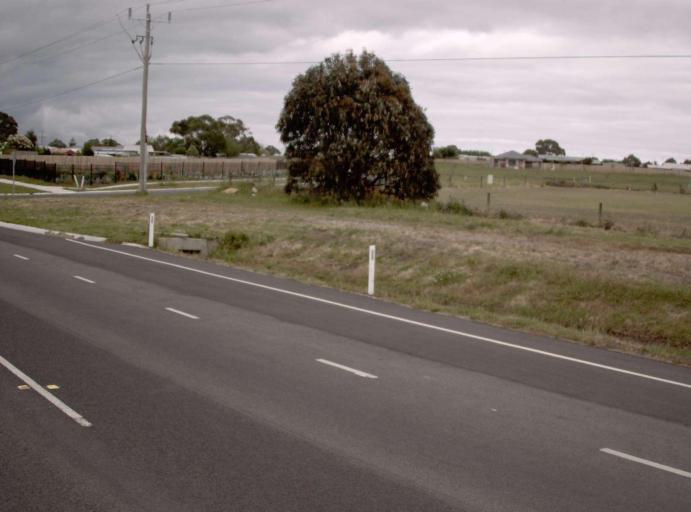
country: AU
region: Victoria
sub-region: Bass Coast
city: North Wonthaggi
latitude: -38.5942
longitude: 145.6079
